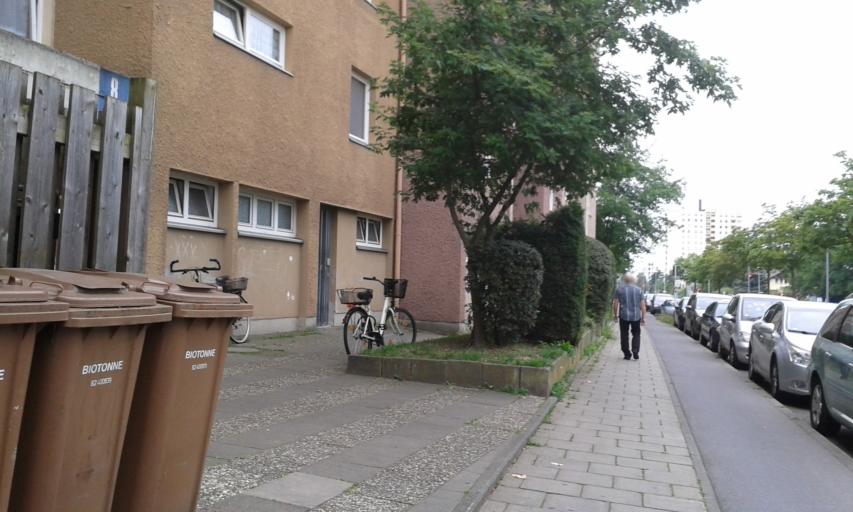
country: DE
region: Bavaria
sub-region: Upper Franconia
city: Bamberg
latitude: 49.8998
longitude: 10.9167
